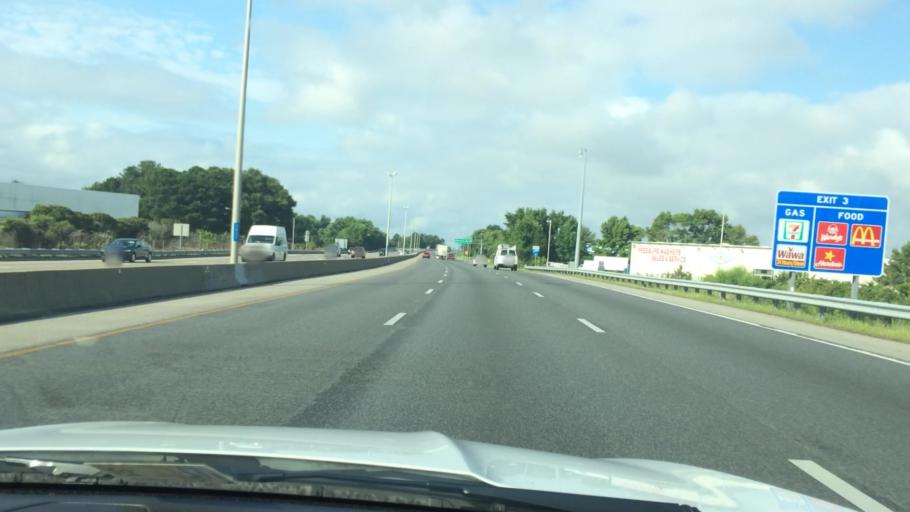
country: US
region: Virginia
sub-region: City of Newport News
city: Newport News
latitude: 37.0096
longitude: -76.3980
